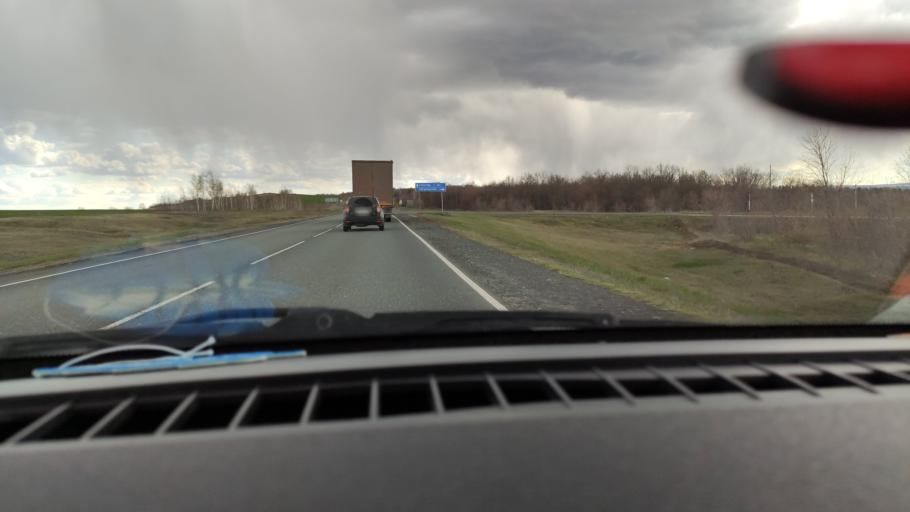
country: RU
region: Saratov
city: Balakovo
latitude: 52.1749
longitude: 47.8350
